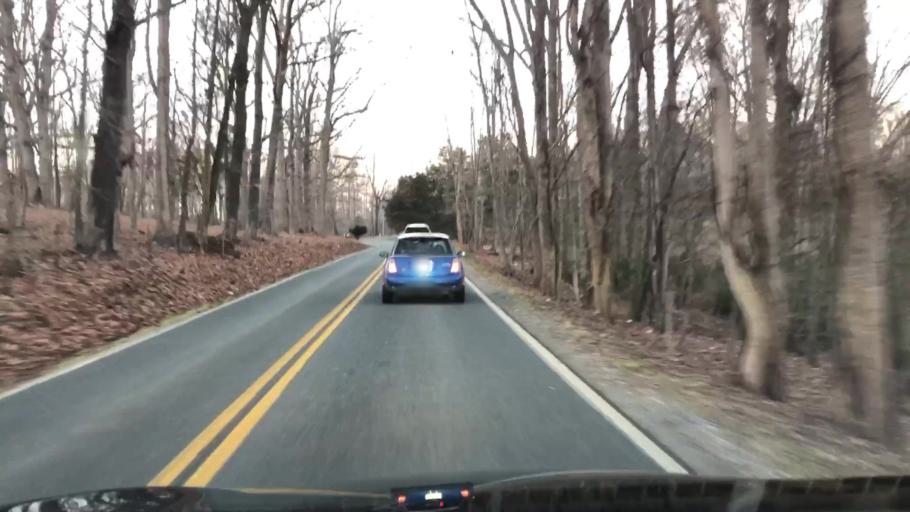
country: US
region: Virginia
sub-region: City of Lynchburg
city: West Lynchburg
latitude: 37.4278
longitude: -79.2496
